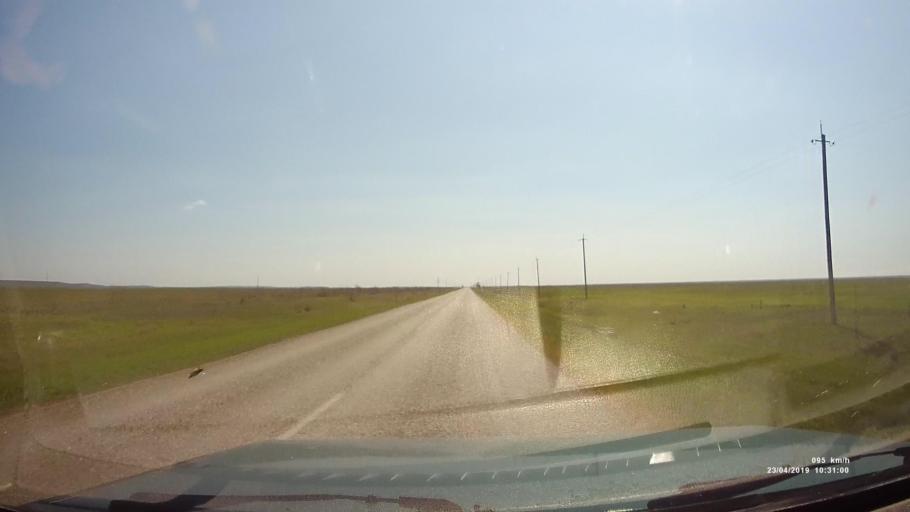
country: RU
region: Kalmykiya
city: Yashalta
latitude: 46.5885
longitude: 42.5548
